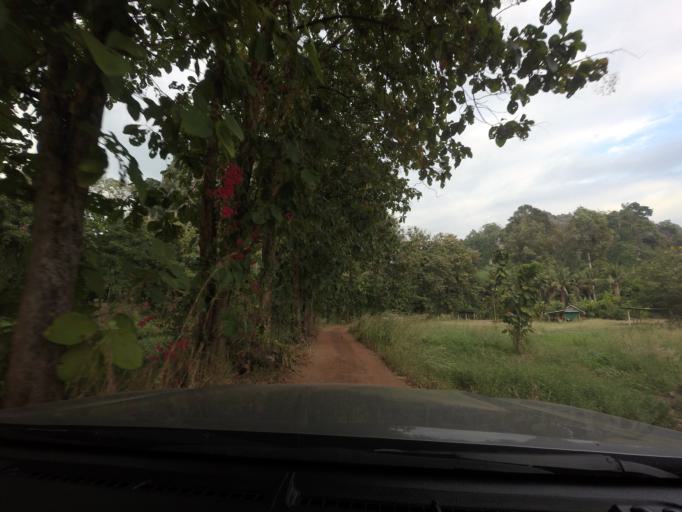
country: TH
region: Phitsanulok
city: Noen Maprang
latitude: 16.5831
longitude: 100.6841
